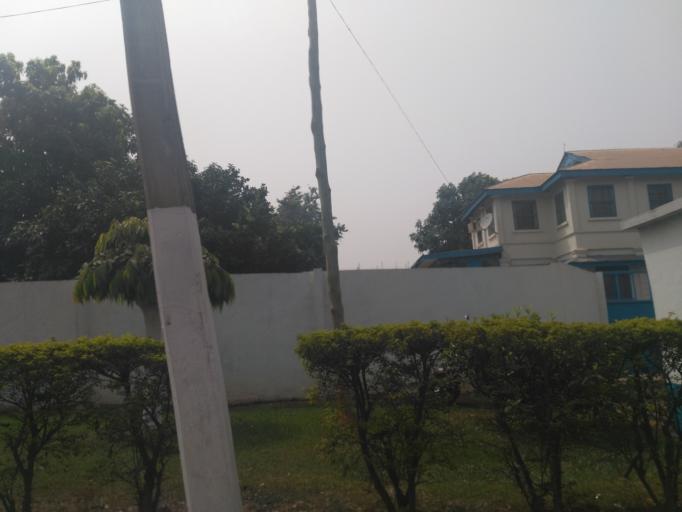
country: GH
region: Ashanti
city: Kumasi
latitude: 6.6860
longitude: -1.6294
